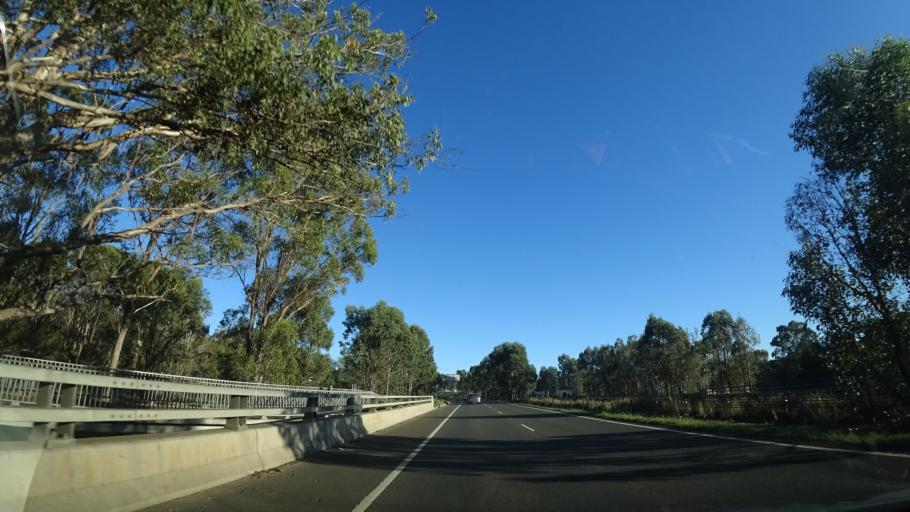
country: AU
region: New South Wales
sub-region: Blacktown
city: Rouse Hill
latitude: -33.6778
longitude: 150.9129
